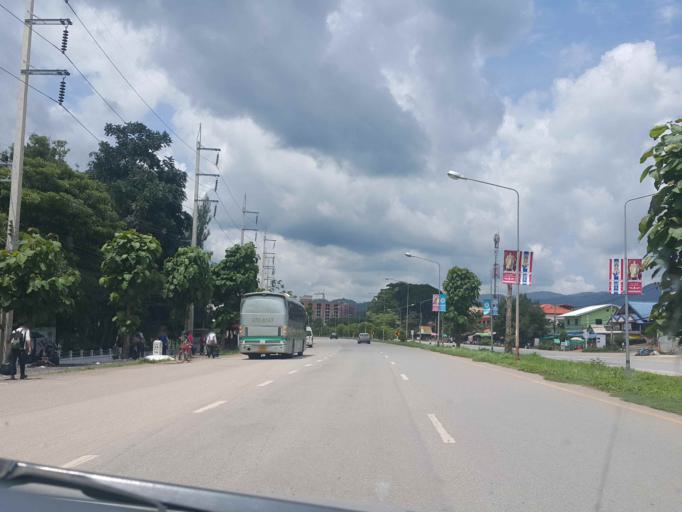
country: TH
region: Phayao
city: Dok Kham Tai
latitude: 19.0272
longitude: 99.9241
